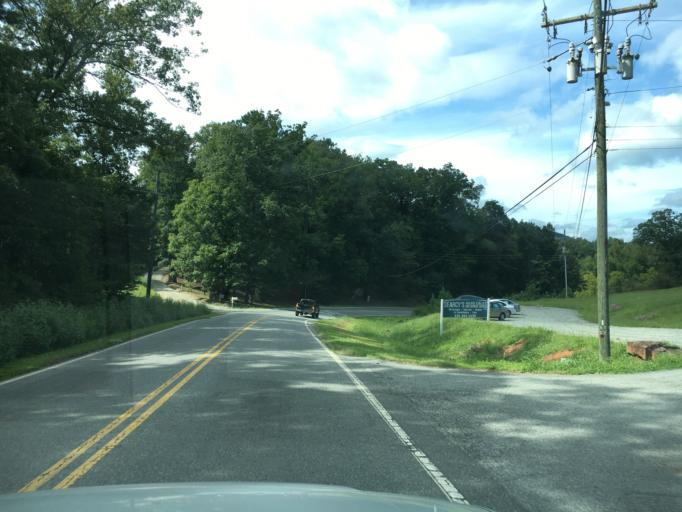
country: US
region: North Carolina
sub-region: Polk County
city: Columbus
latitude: 35.2672
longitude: -82.1829
